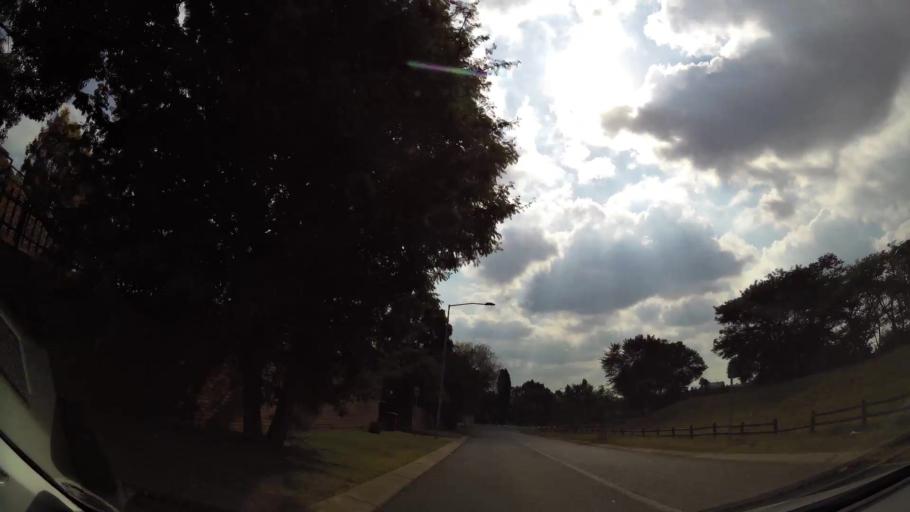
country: ZA
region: Gauteng
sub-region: City of Tshwane Metropolitan Municipality
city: Pretoria
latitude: -25.7596
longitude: 28.3083
